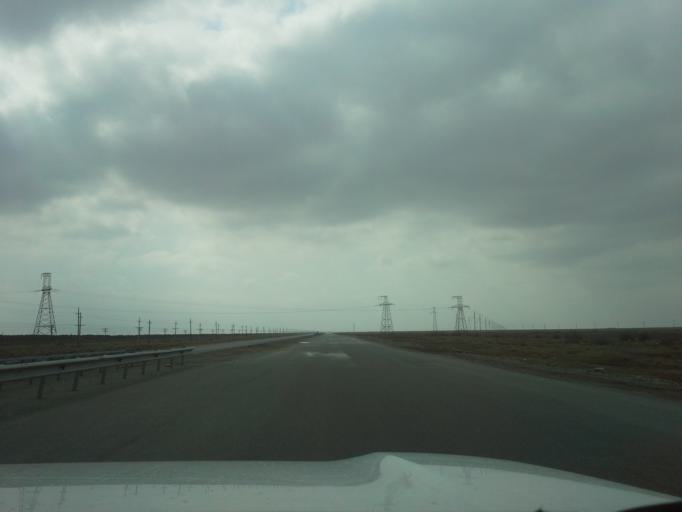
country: IR
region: Razavi Khorasan
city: Kalat-e Naderi
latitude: 37.2157
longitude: 60.0952
